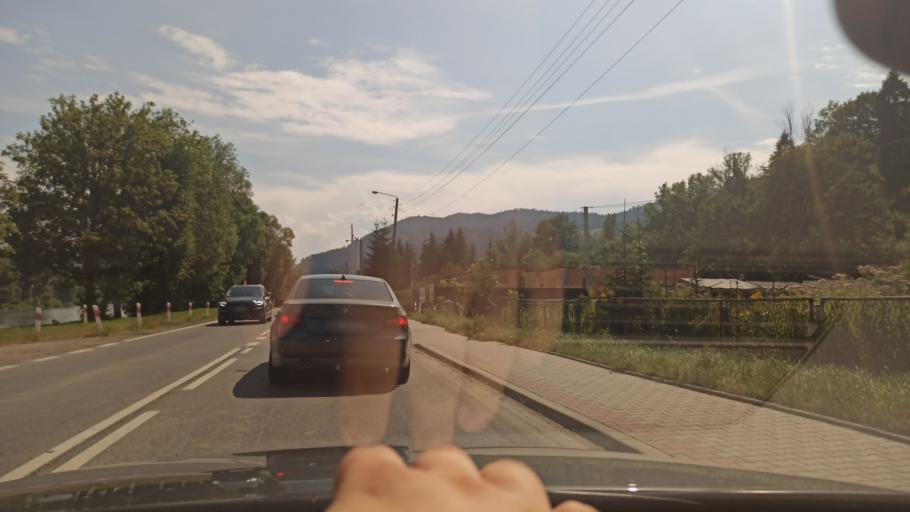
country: PL
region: Lesser Poland Voivodeship
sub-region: Powiat nowotarski
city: Kroscienko nad Dunajcem
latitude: 49.4479
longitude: 20.4229
